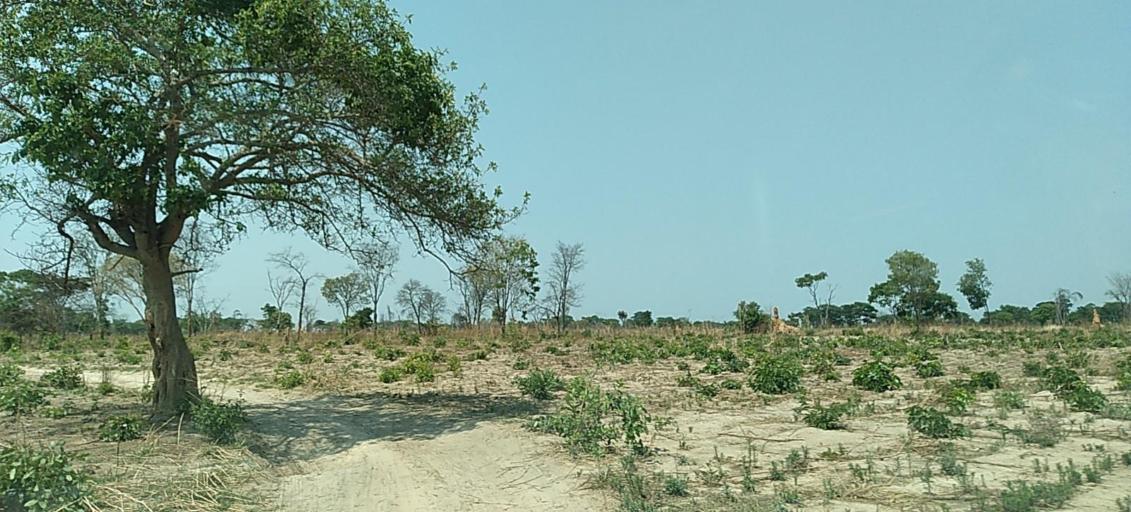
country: ZM
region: Copperbelt
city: Mpongwe
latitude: -13.8638
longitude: 28.0540
